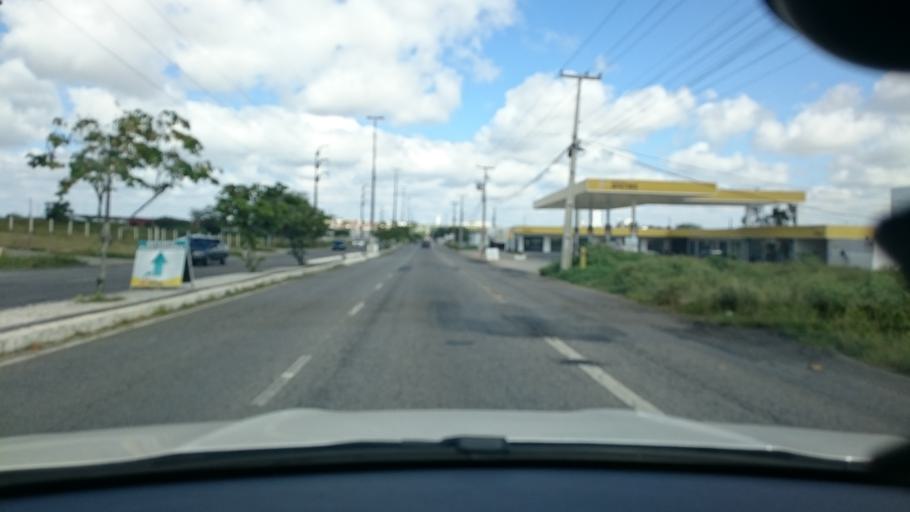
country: BR
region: Paraiba
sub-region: Campina Grande
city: Campina Grande
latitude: -7.2329
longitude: -35.9136
